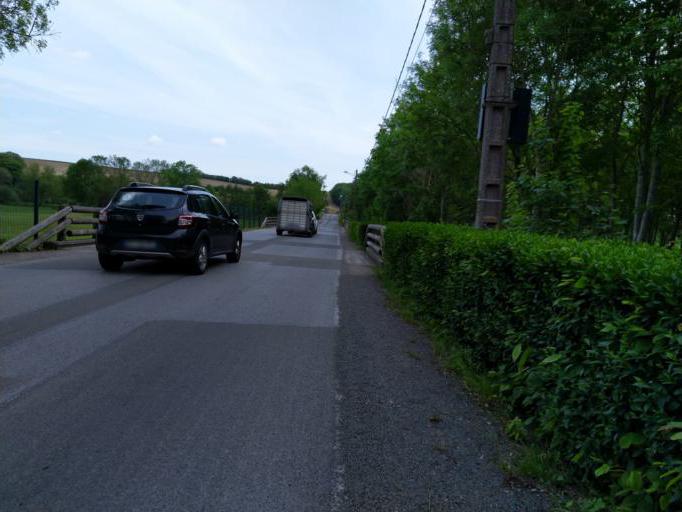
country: FR
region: Picardie
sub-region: Departement de l'Aisne
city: Guise
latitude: 49.9265
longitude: 3.5778
